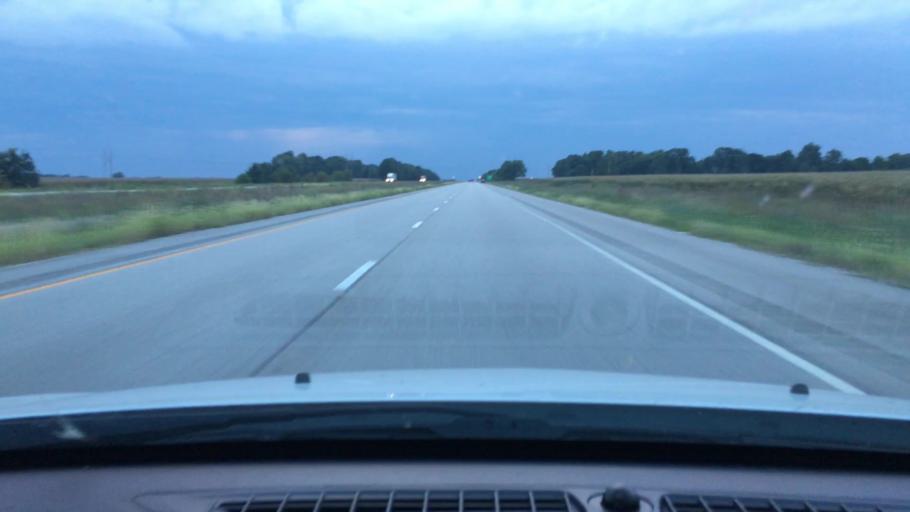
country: US
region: Illinois
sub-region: Sangamon County
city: New Berlin
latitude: 39.7371
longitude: -90.0067
